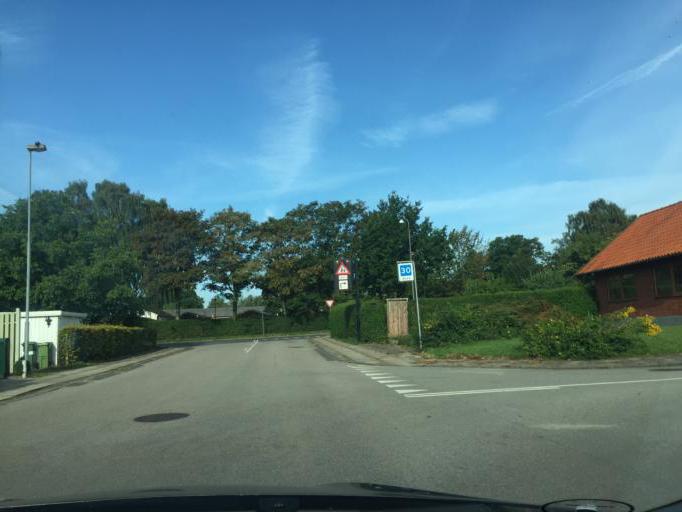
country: DK
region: South Denmark
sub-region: Odense Kommune
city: Bellinge
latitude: 55.3689
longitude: 10.3485
